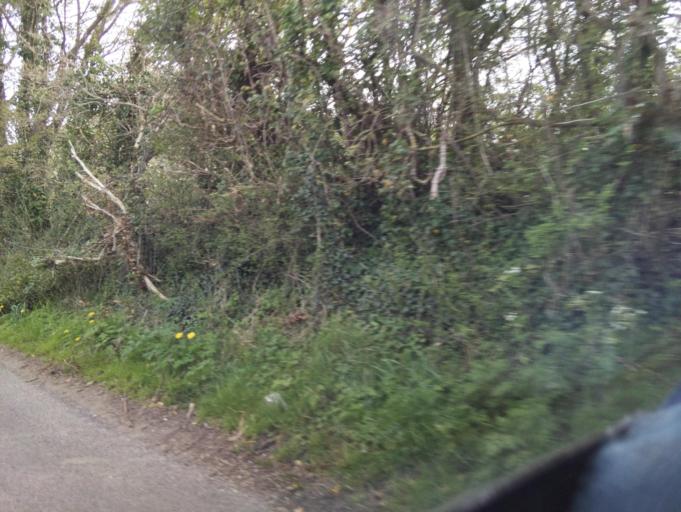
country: GB
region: England
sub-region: Dorset
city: Sherborne
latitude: 50.9560
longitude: -2.5068
